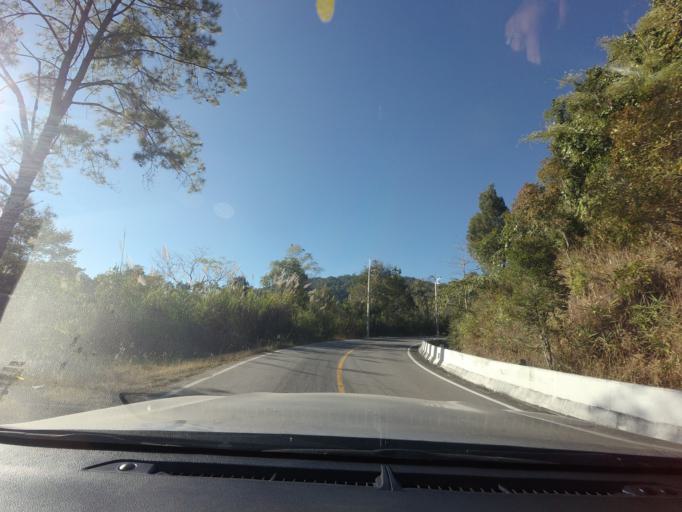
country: TH
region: Mae Hong Son
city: Mae Hi
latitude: 19.2186
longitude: 98.6726
